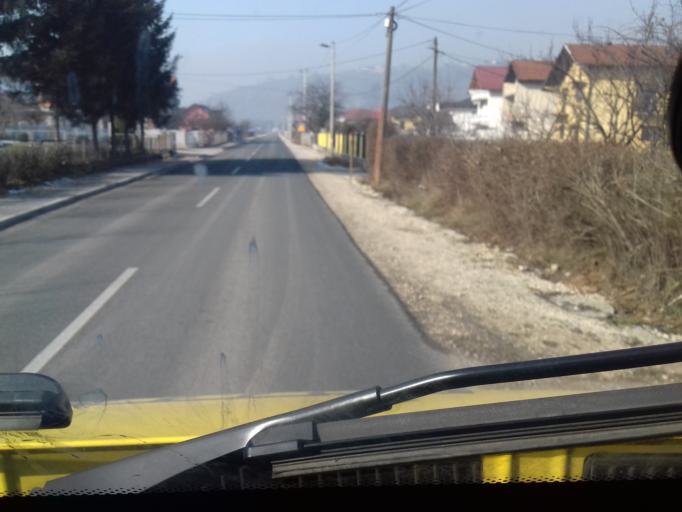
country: BA
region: Federation of Bosnia and Herzegovina
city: Ilijas
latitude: 43.9361
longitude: 18.2973
